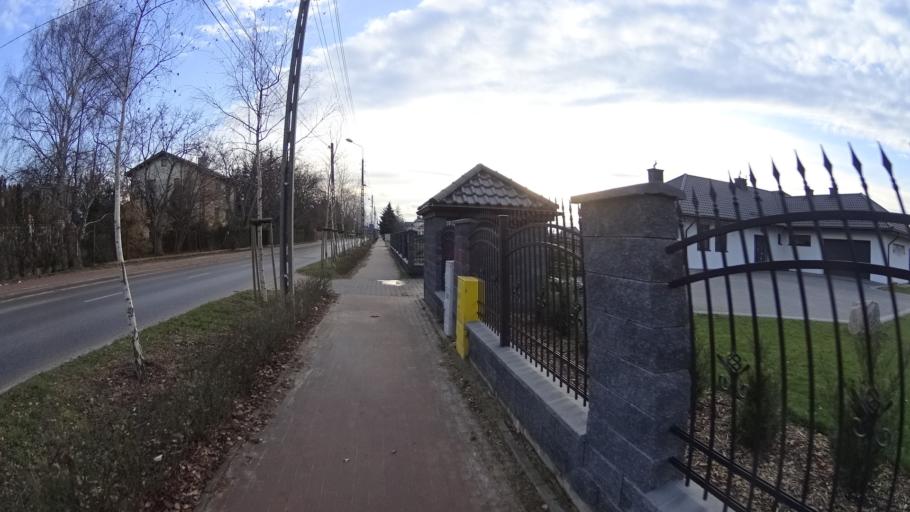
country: PL
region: Masovian Voivodeship
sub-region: Powiat warszawski zachodni
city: Ozarow Mazowiecki
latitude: 52.2241
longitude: 20.8013
